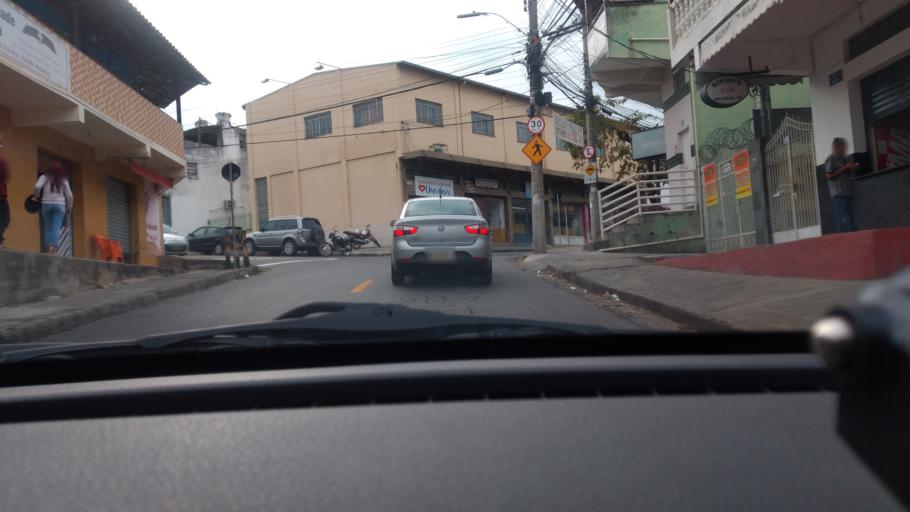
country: BR
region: Minas Gerais
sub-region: Santa Luzia
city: Santa Luzia
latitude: -19.8115
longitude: -43.9395
